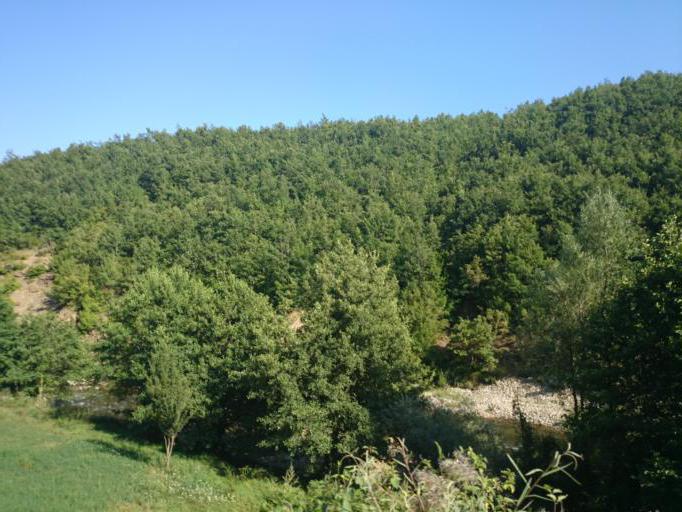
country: AL
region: Diber
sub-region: Rrethi i Bulqizes
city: Zerqan
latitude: 41.5144
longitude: 20.3881
